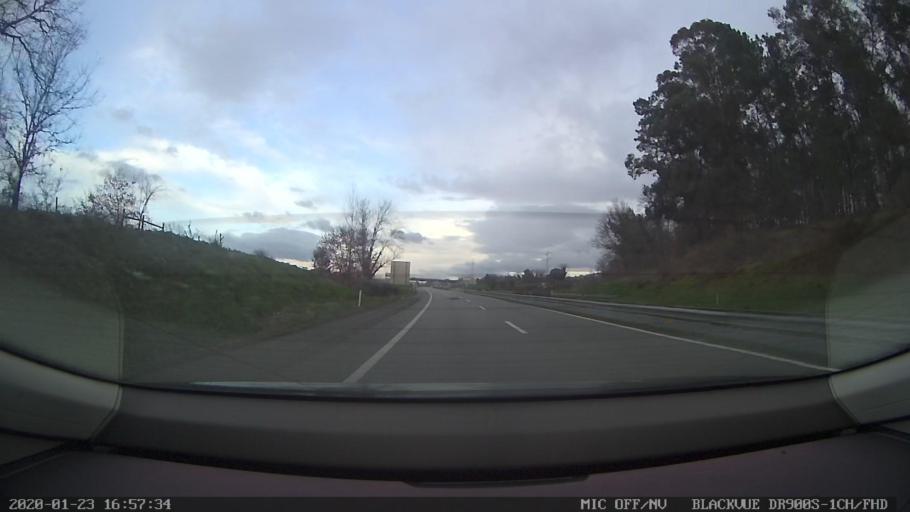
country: PT
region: Porto
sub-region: Penafiel
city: Penafiel
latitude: 41.2038
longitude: -8.3031
